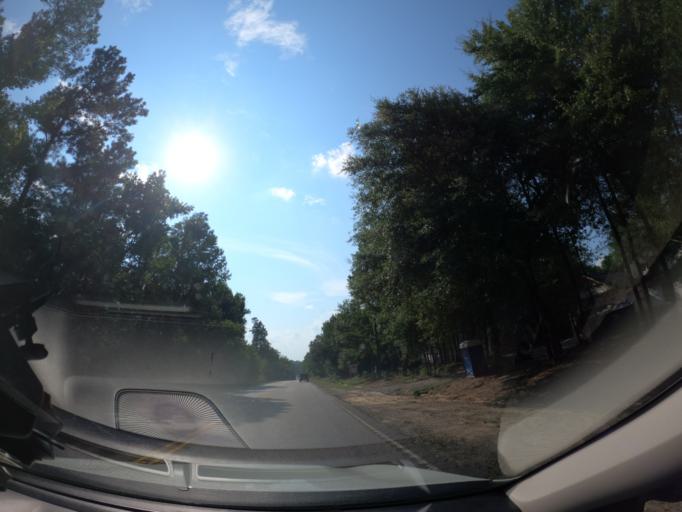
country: US
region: South Carolina
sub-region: Aiken County
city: Clearwater
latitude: 33.4248
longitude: -81.8673
